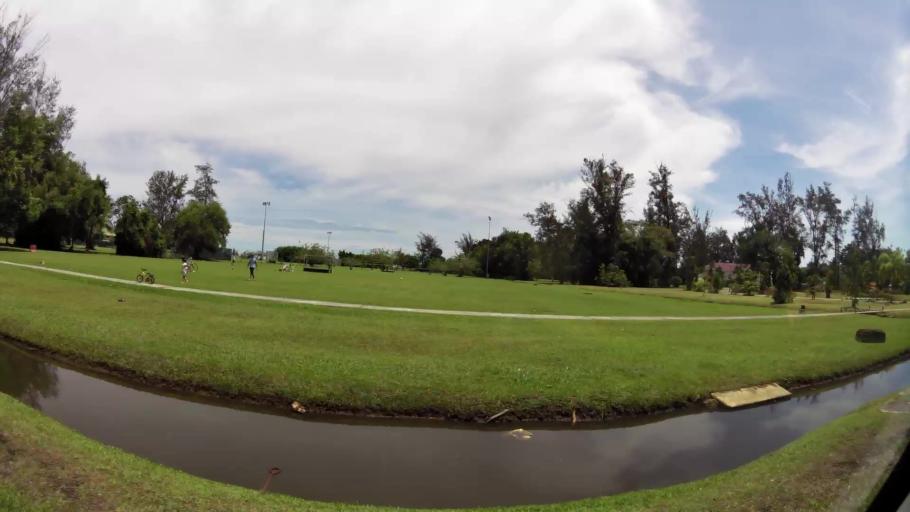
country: BN
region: Belait
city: Kuala Belait
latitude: 4.6004
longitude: 114.2723
